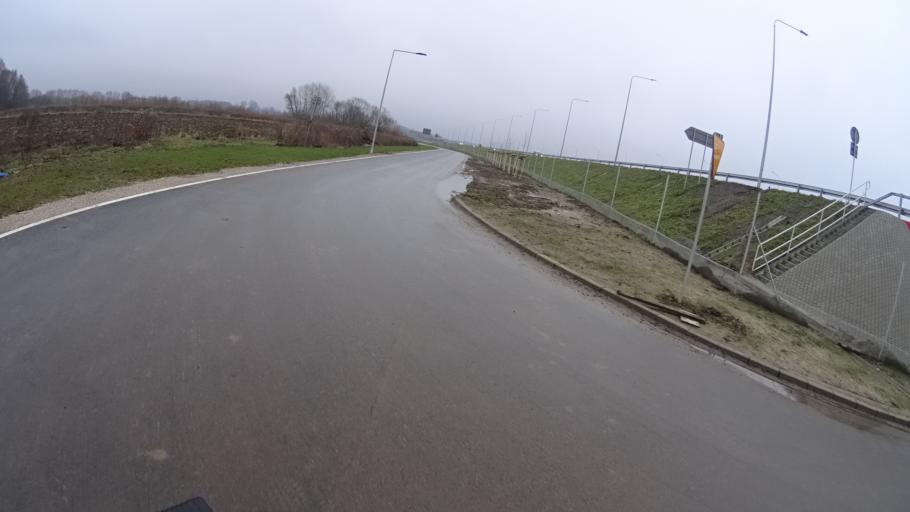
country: PL
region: Masovian Voivodeship
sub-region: Warszawa
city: Wilanow
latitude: 52.1519
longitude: 21.0967
